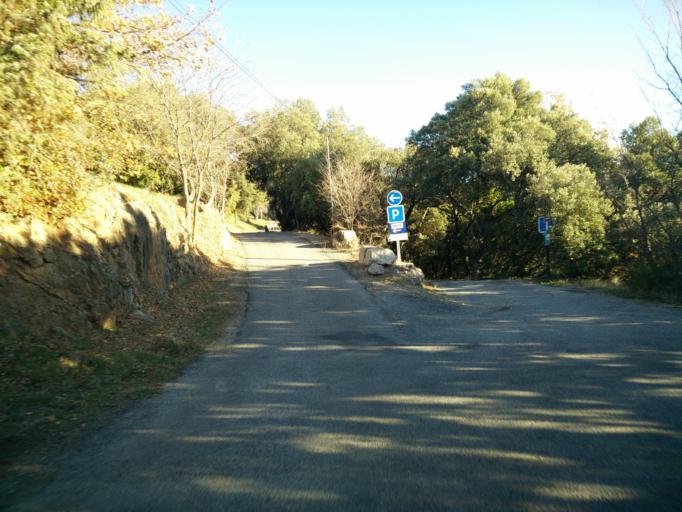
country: FR
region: Provence-Alpes-Cote d'Azur
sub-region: Departement du Var
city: Villecroze
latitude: 43.5877
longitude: 6.3043
